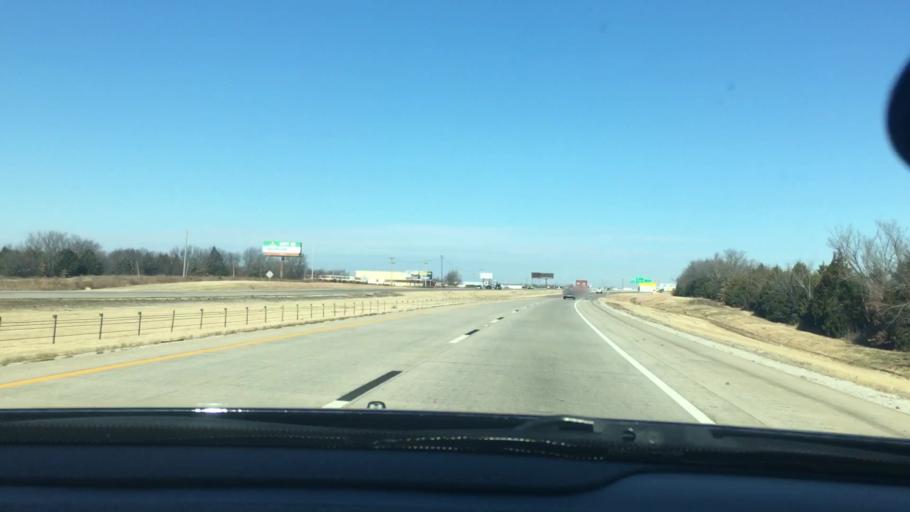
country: US
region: Oklahoma
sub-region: Carter County
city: Ardmore
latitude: 34.1624
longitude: -97.1655
